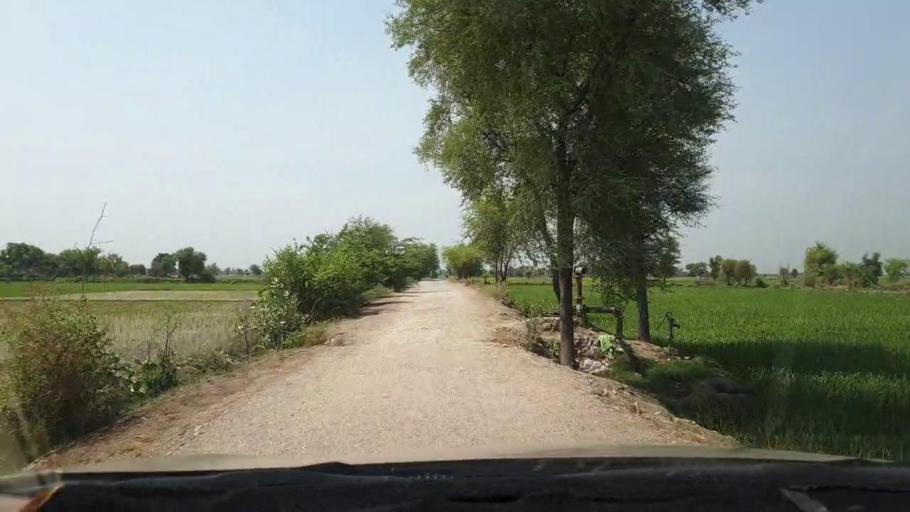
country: PK
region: Sindh
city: Naudero
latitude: 27.6425
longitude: 68.2744
